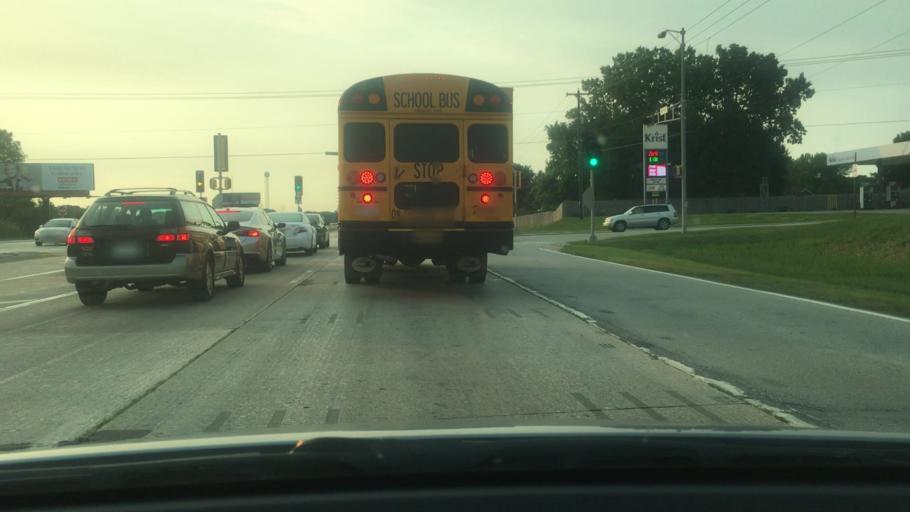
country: US
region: Wisconsin
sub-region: Brown County
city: Ashwaubenon
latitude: 44.4924
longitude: -88.0985
